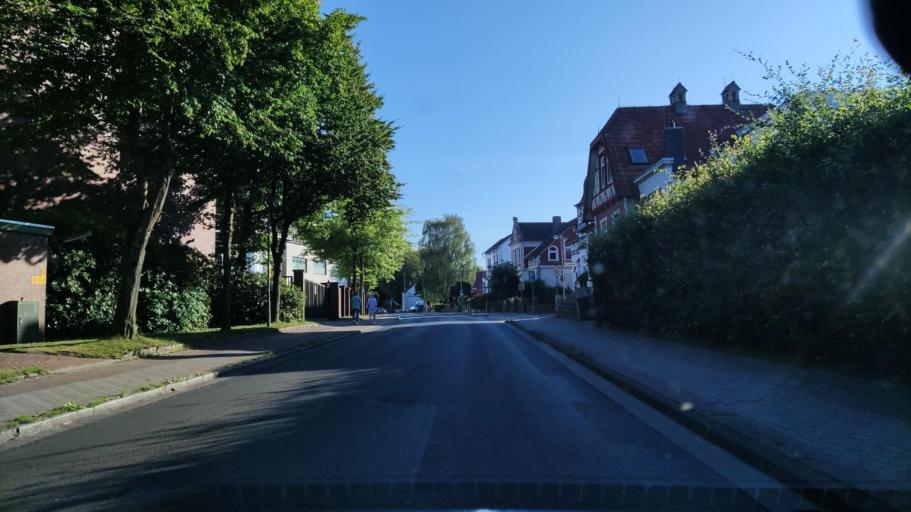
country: DE
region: Lower Saxony
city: Jever
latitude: 53.5769
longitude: 7.9016
